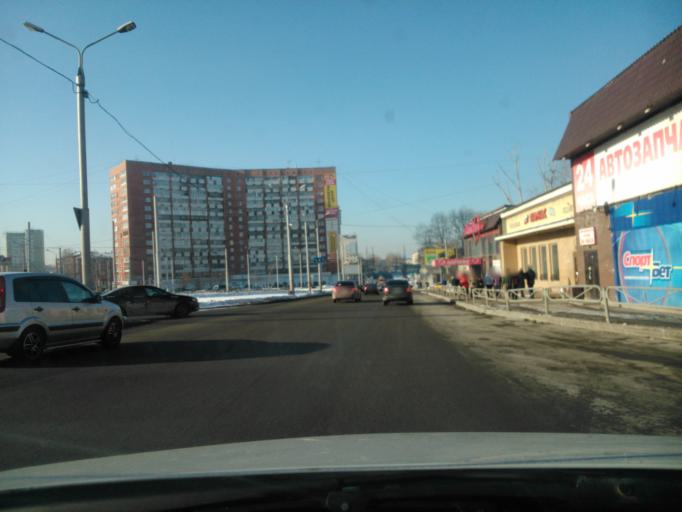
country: RU
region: Perm
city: Perm
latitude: 57.9866
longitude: 56.2154
